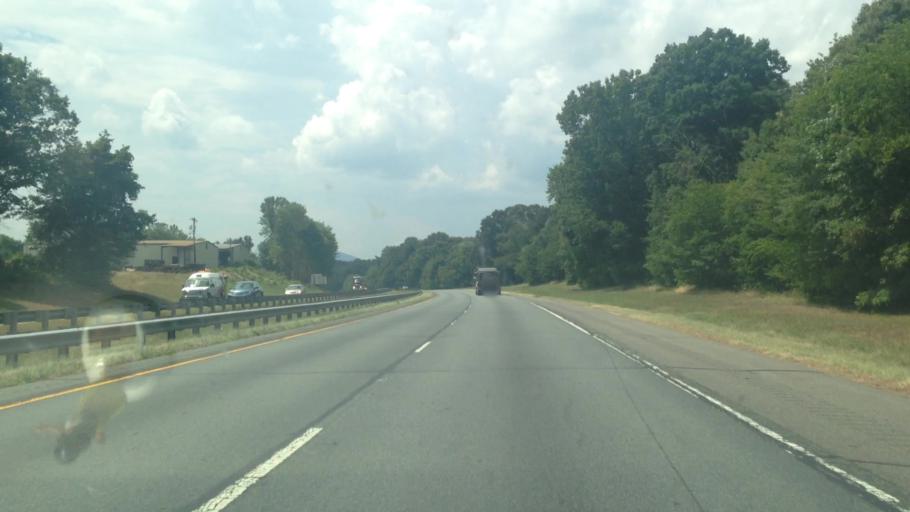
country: US
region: North Carolina
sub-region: Stokes County
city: King
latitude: 36.2743
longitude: -80.3787
